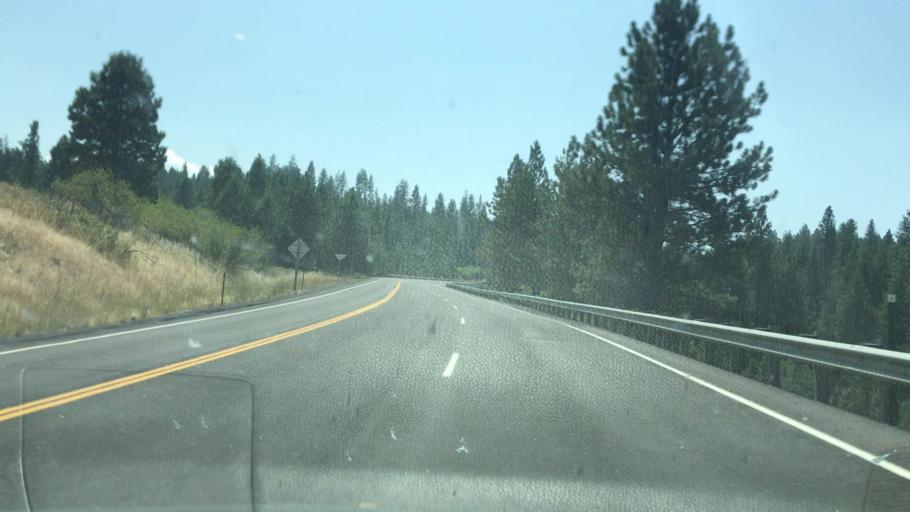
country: US
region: Idaho
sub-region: Idaho County
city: Grangeville
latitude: 45.8696
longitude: -116.2366
